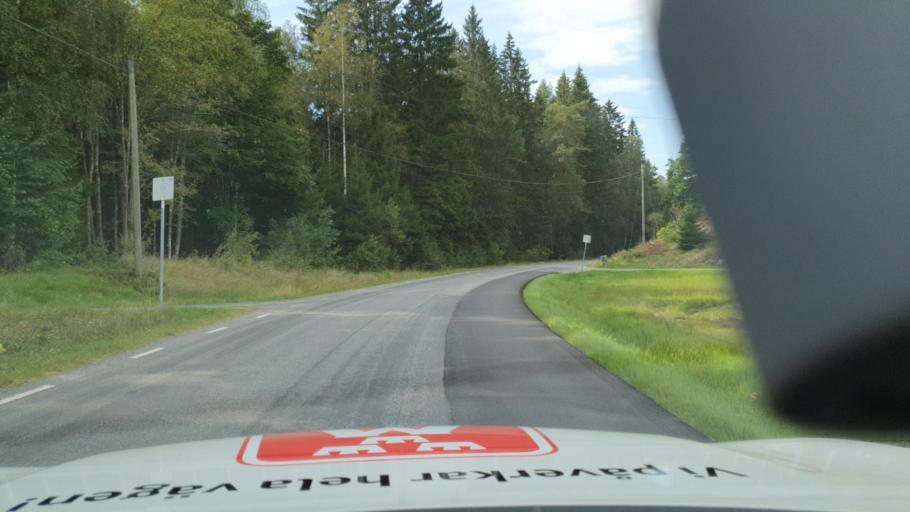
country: SE
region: Vaestra Goetaland
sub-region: Marks Kommun
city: Kinna
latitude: 57.3886
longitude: 12.7015
